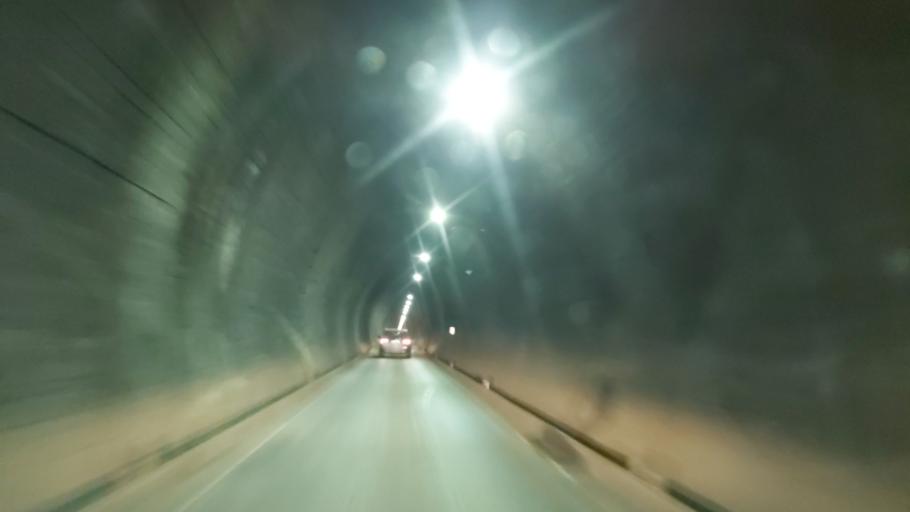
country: CL
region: Araucania
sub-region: Provincia de Cautin
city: Vilcun
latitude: -38.5260
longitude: -71.5127
